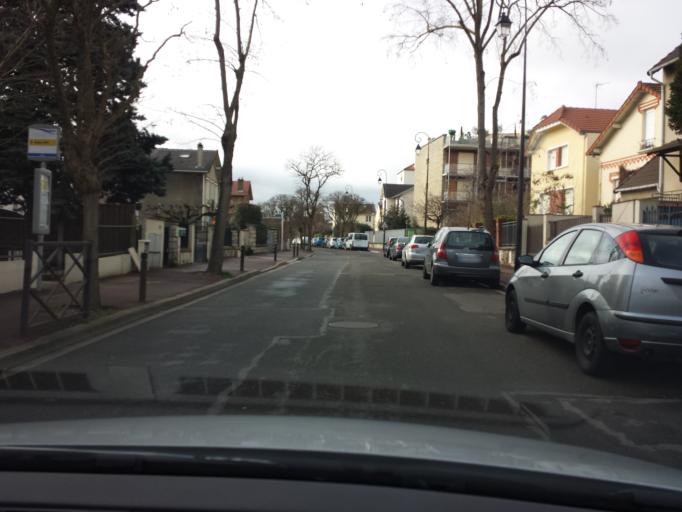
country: FR
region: Ile-de-France
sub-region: Departement des Hauts-de-Seine
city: Antony
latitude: 48.7510
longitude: 2.2892
